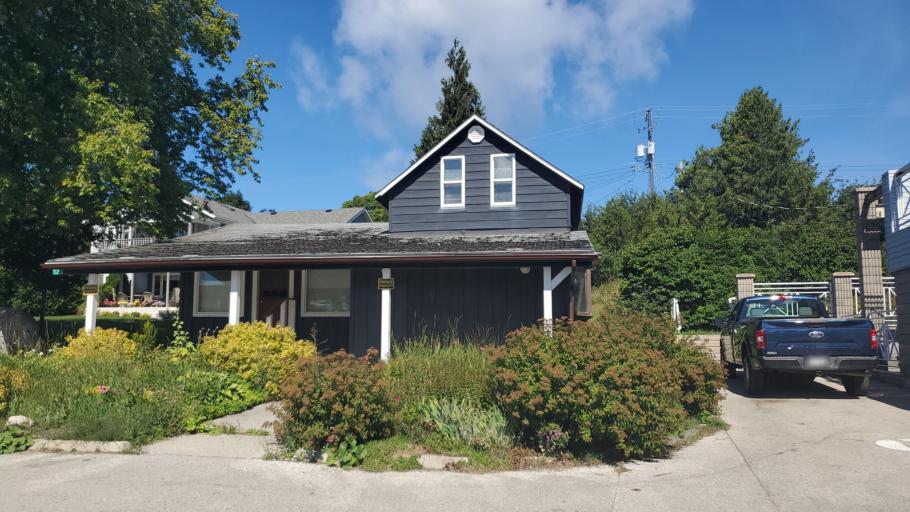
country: CA
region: Ontario
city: Tobermory
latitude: 45.2553
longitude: -81.6645
